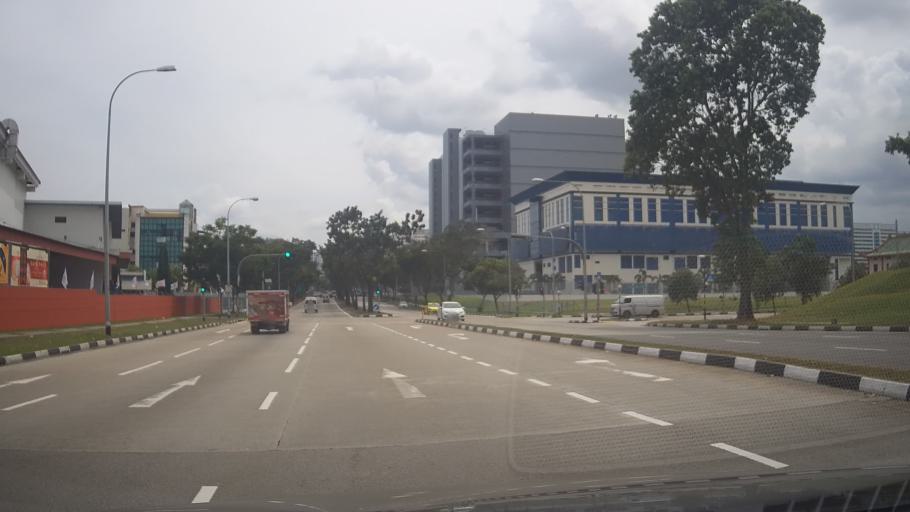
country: MY
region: Johor
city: Johor Bahru
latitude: 1.4538
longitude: 103.8015
